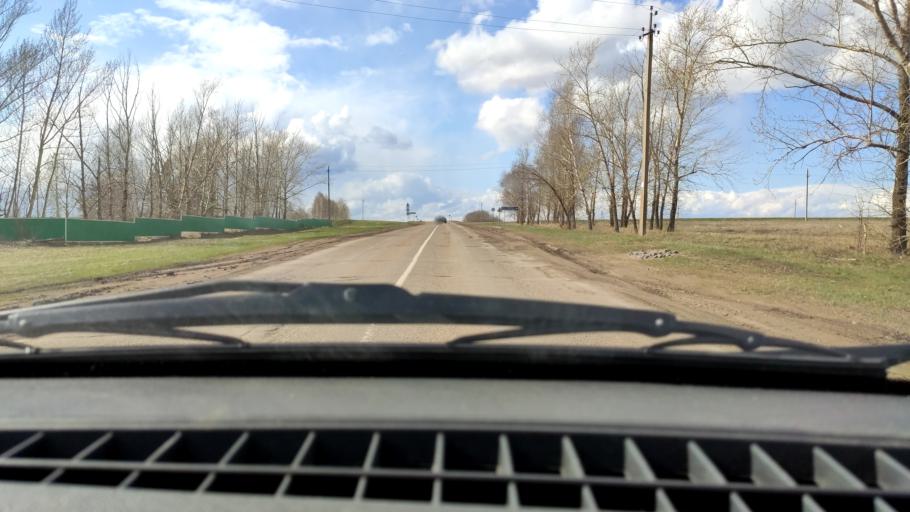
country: RU
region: Bashkortostan
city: Kushnarenkovo
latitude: 55.0951
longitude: 55.0531
